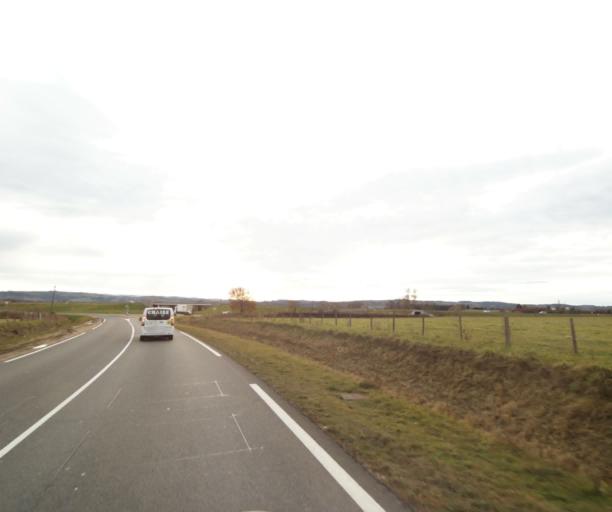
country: FR
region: Rhone-Alpes
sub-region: Departement de la Loire
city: Sury-le-Comtal
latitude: 45.5139
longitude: 4.1909
